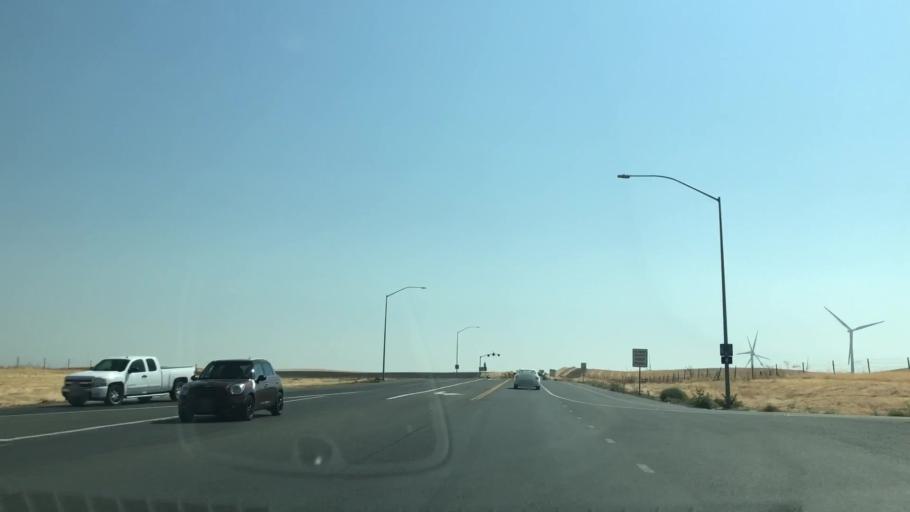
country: US
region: California
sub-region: Solano County
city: Rio Vista
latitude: 38.1834
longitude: -121.8052
